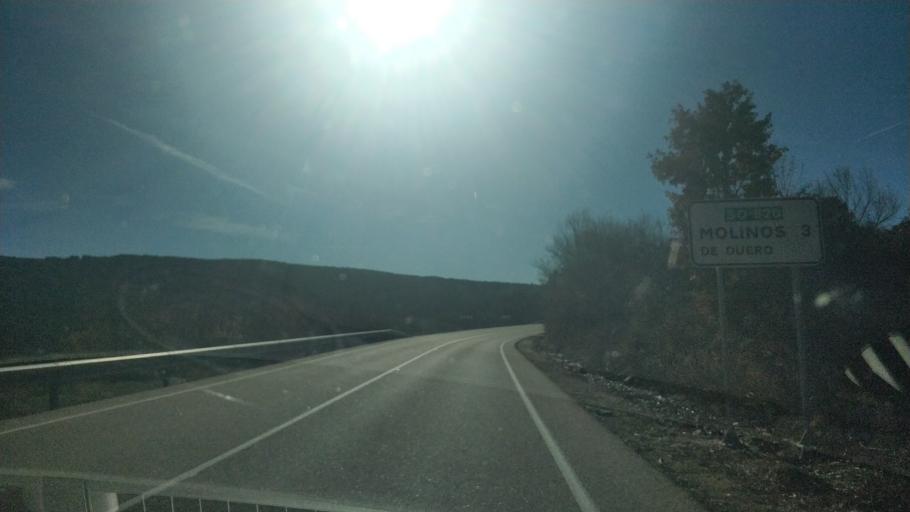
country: ES
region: Castille and Leon
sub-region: Provincia de Soria
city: Vinuesa
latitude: 41.9030
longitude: -2.7663
